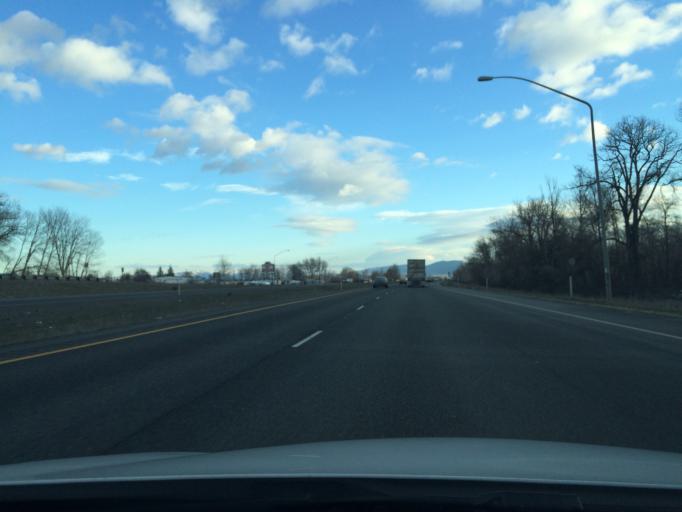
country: US
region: Washington
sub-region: Kittitas County
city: Ellensburg
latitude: 47.0050
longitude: -120.5901
